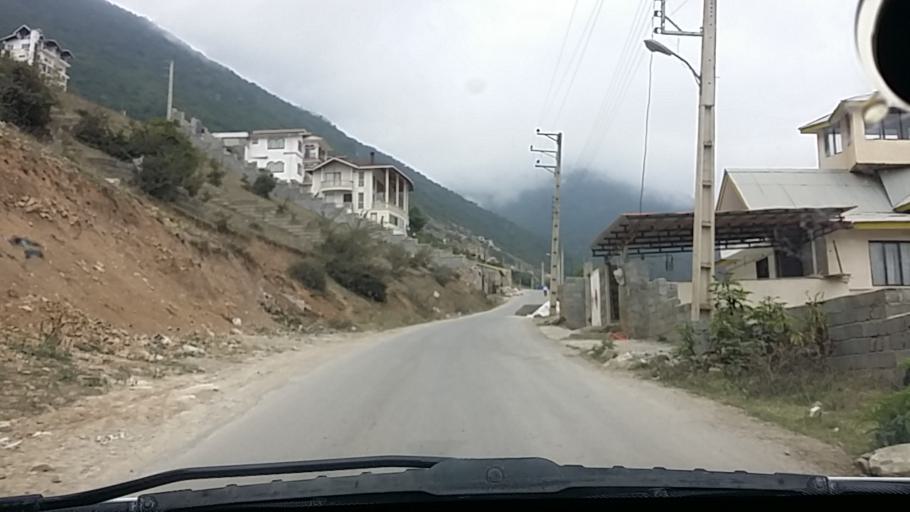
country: IR
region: Mazandaran
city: `Abbasabad
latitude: 36.4764
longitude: 51.1400
